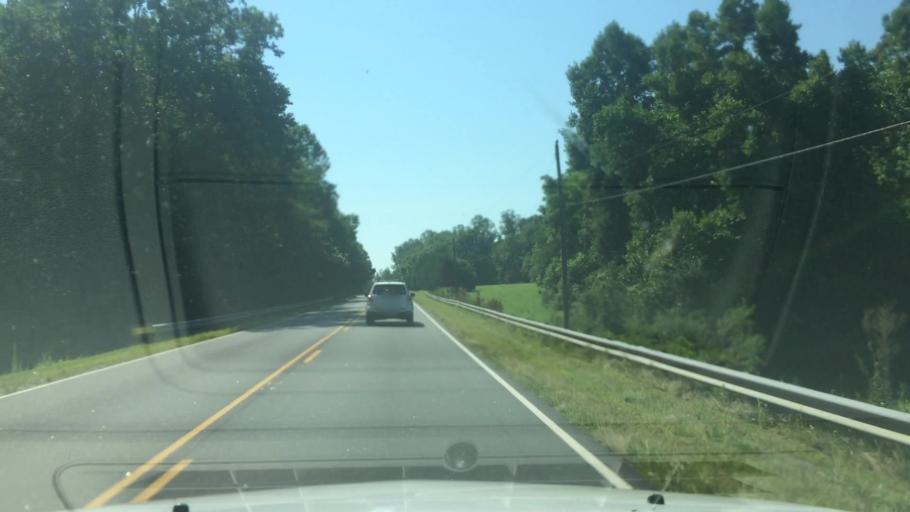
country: US
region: North Carolina
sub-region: Caldwell County
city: Hudson
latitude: 35.9142
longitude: -81.4477
